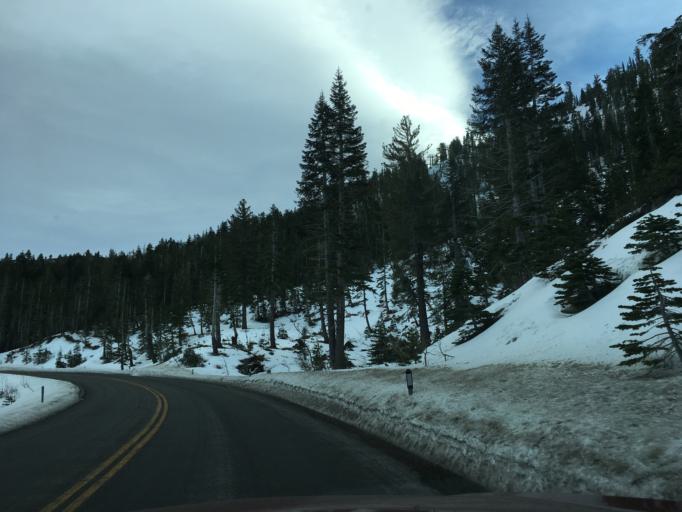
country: US
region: Nevada
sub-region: Washoe County
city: Incline Village
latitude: 39.3252
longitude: -119.8755
